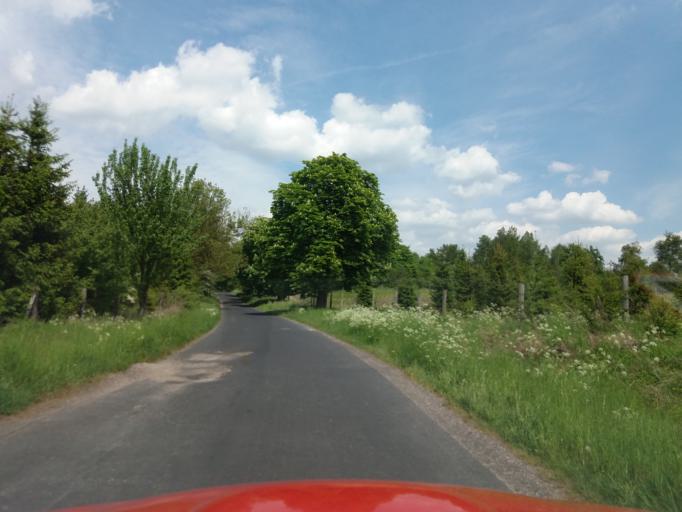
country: PL
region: West Pomeranian Voivodeship
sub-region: Powiat choszczenski
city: Bierzwnik
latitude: 53.1074
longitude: 15.6327
